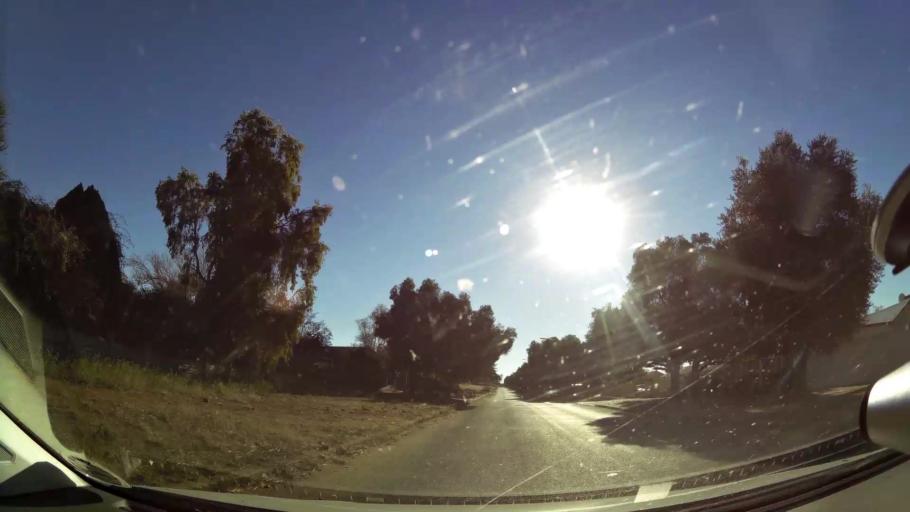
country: ZA
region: Northern Cape
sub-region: Frances Baard District Municipality
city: Kimberley
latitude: -28.7575
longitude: 24.7758
